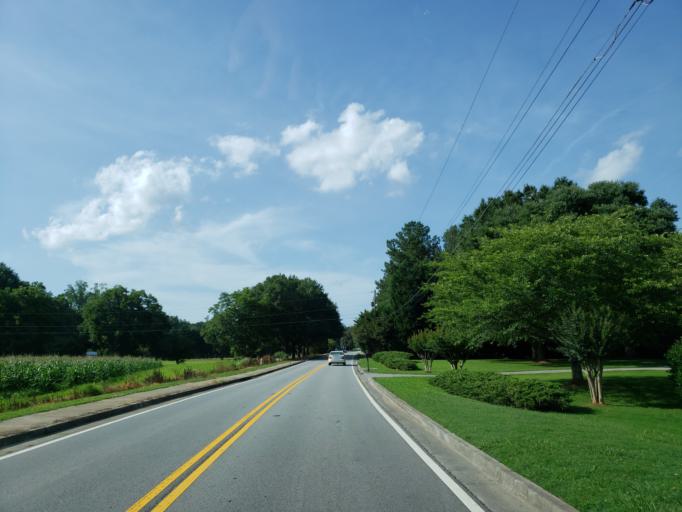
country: US
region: Georgia
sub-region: Cobb County
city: Powder Springs
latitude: 33.8983
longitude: -84.6873
